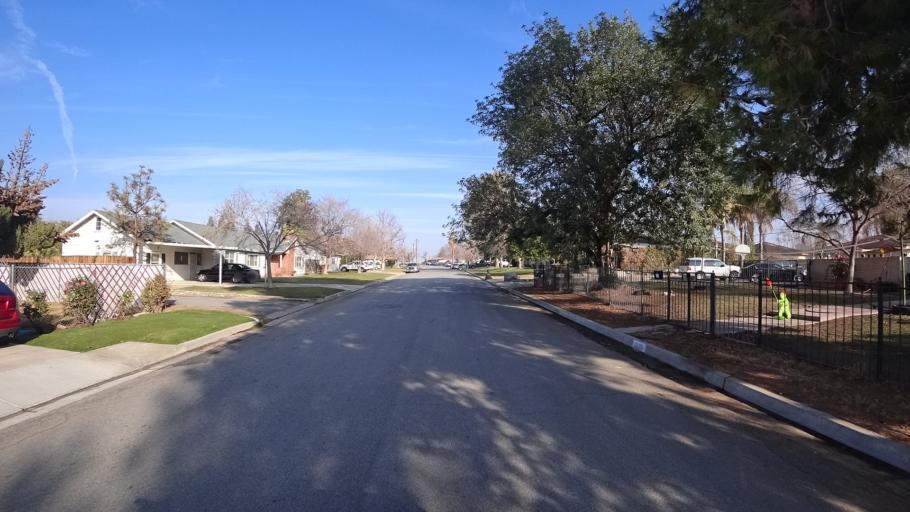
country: US
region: California
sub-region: Kern County
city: Oildale
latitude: 35.4061
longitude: -118.9904
